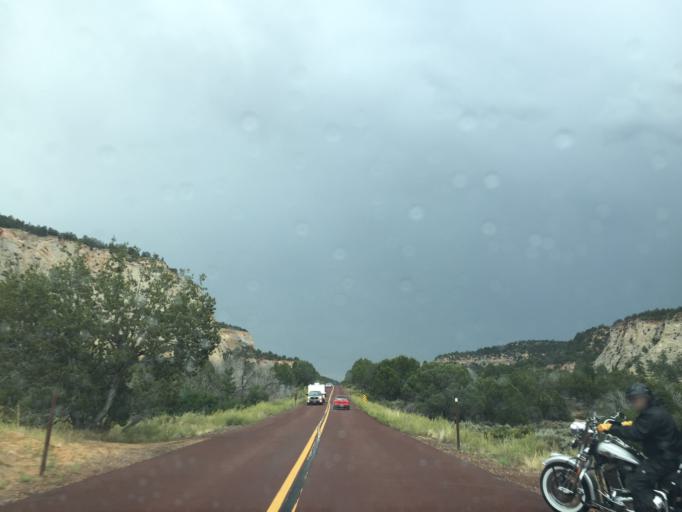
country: US
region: Utah
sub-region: Washington County
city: Hildale
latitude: 37.2343
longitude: -112.8703
